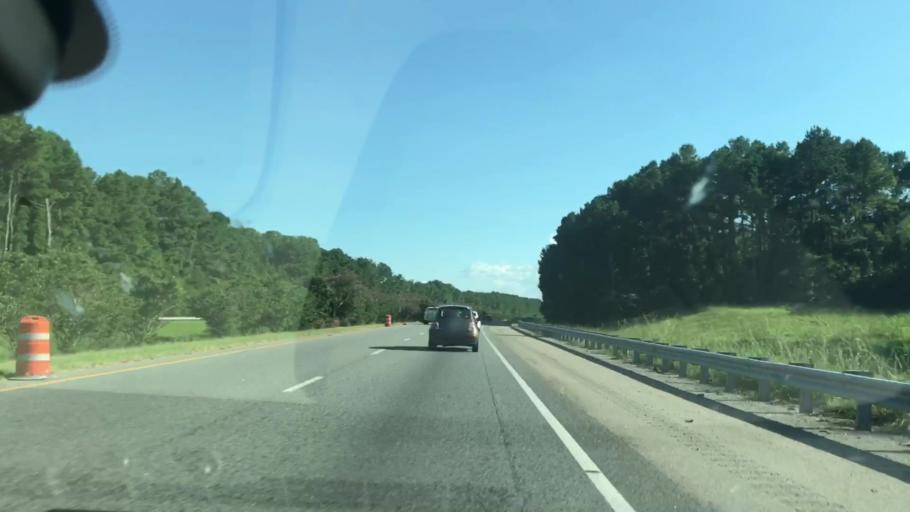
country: US
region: Georgia
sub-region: Harris County
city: Hamilton
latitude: 32.7870
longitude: -85.0205
